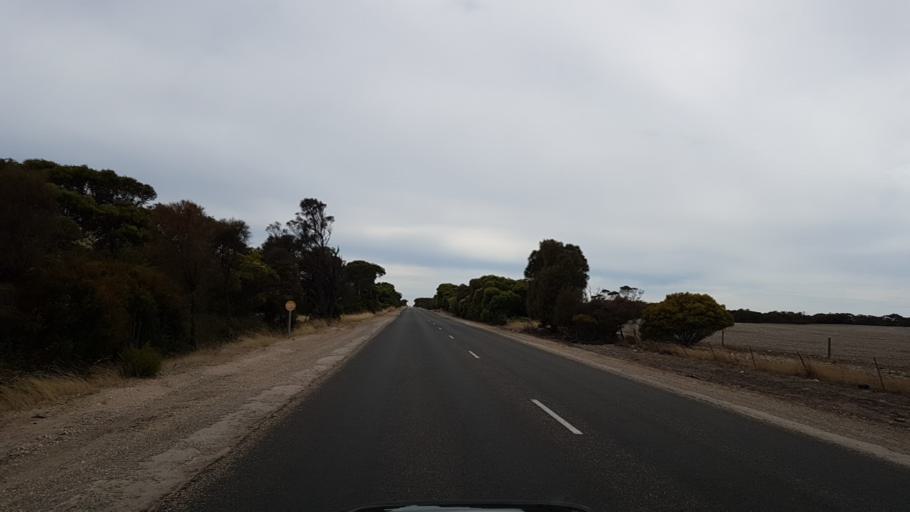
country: AU
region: South Australia
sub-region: Yorke Peninsula
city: Honiton
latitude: -34.9881
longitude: 137.1387
